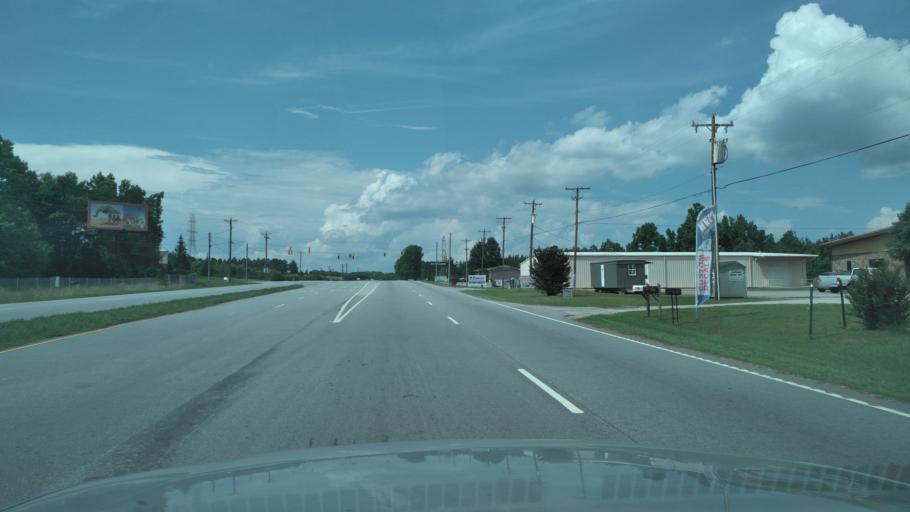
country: US
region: South Carolina
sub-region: Spartanburg County
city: Roebuck
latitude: 34.8469
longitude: -81.9677
